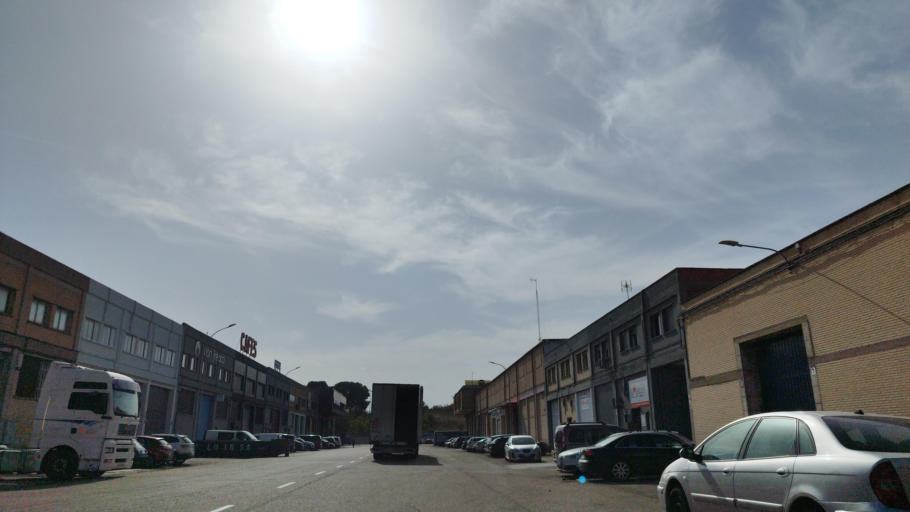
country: ES
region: Aragon
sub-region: Provincia de Zaragoza
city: Oliver-Valdefierro, Oliver, Valdefierro
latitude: 41.6730
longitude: -0.9464
